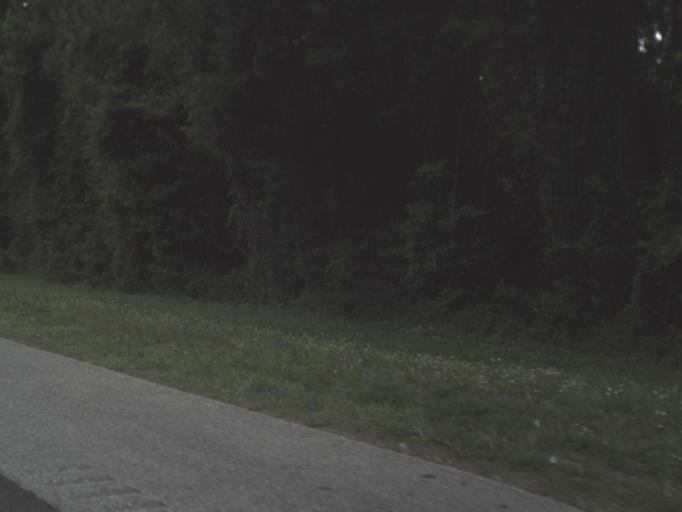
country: US
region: Florida
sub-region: Saint Johns County
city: Fruit Cove
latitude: 30.1682
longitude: -81.5846
